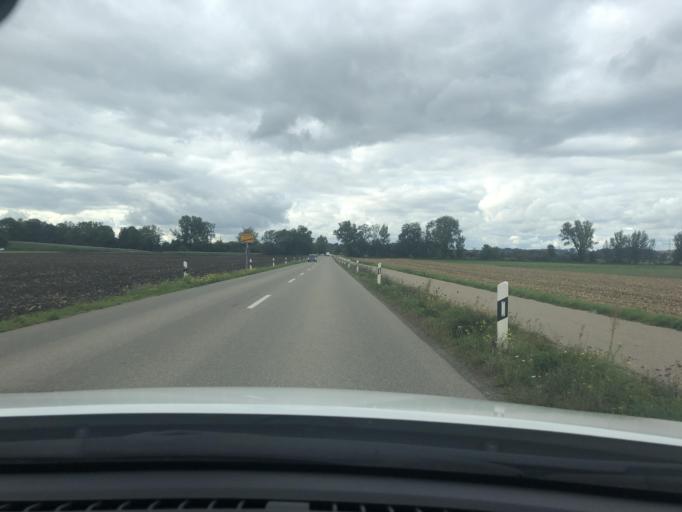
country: DE
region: Bavaria
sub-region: Upper Bavaria
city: Bergkirchen
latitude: 48.2403
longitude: 11.3419
